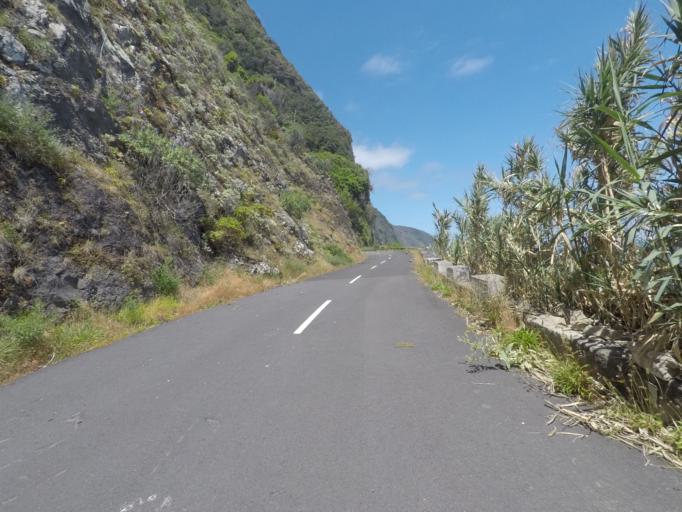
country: PT
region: Madeira
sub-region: Porto Moniz
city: Porto Moniz
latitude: 32.8286
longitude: -17.1271
